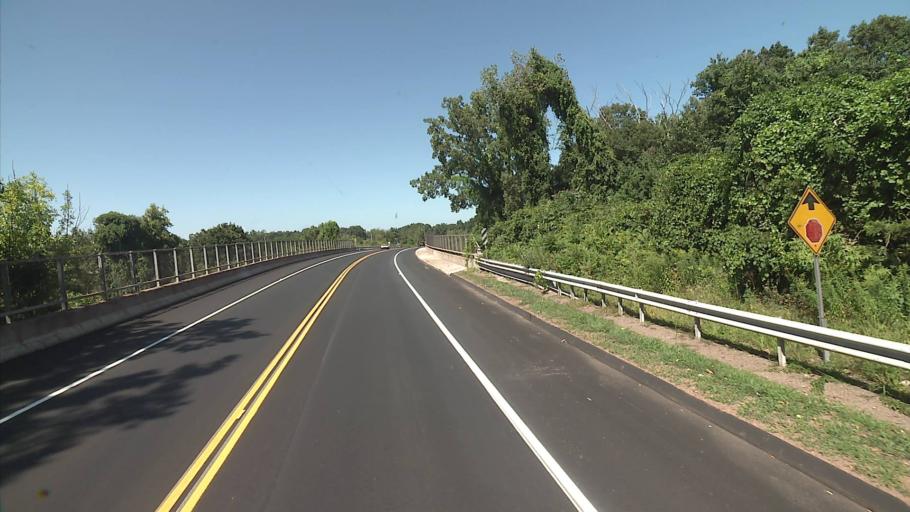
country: US
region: Connecticut
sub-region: Hartford County
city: Windsor Locks
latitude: 41.9104
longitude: -72.6261
